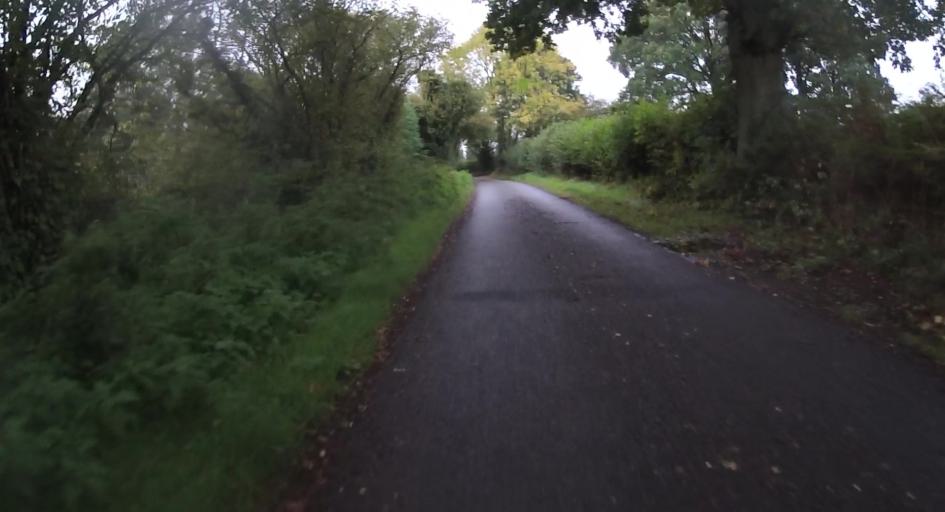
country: GB
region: England
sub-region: Hampshire
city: Tadley
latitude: 51.3496
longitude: -1.1765
